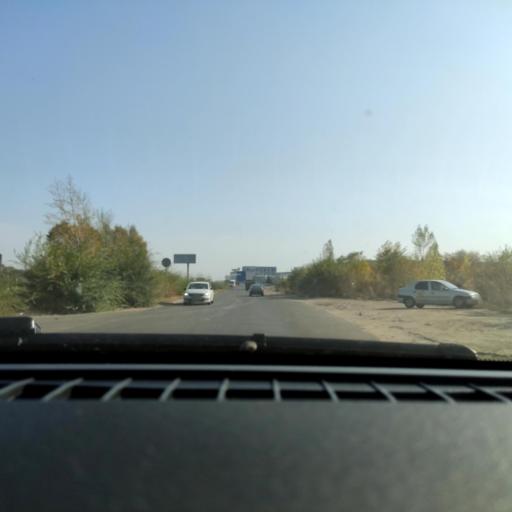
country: RU
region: Voronezj
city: Somovo
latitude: 51.6797
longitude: 39.2866
